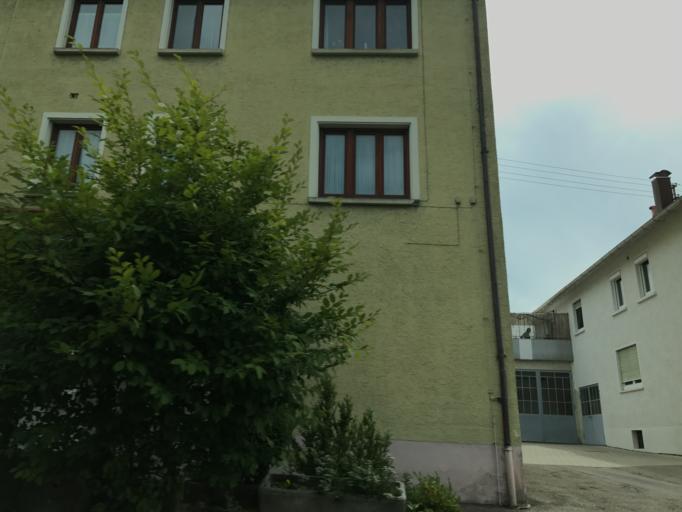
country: DE
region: Baden-Wuerttemberg
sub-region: Tuebingen Region
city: Wolpertswende
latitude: 47.8645
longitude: 9.5862
